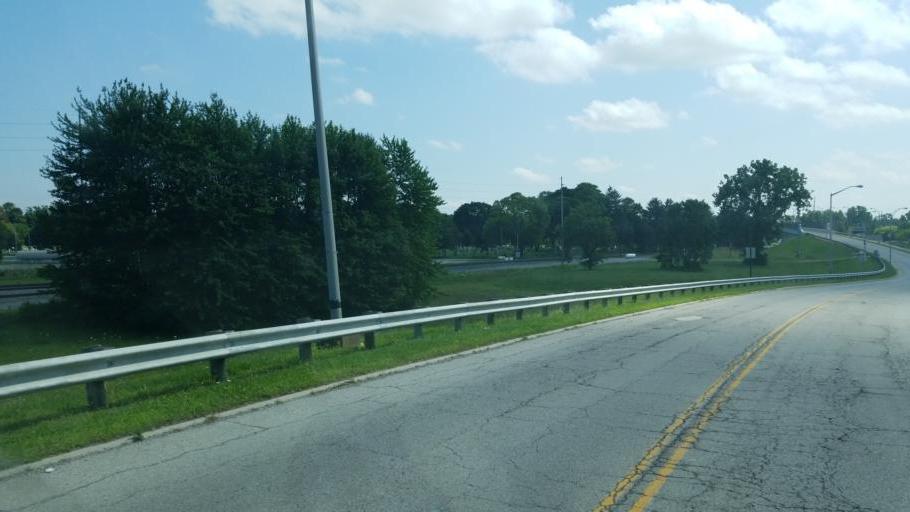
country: US
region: Ohio
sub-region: Huron County
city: Bellevue
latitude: 41.2690
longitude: -82.8392
